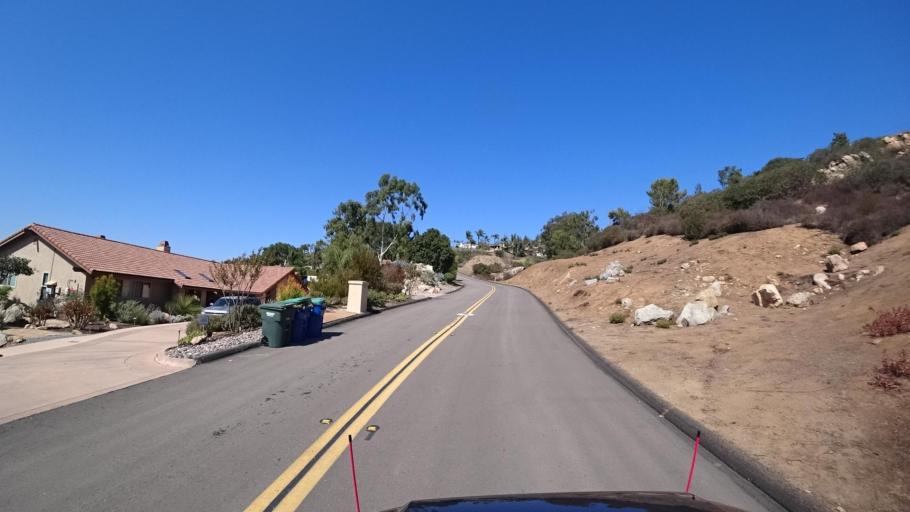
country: US
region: California
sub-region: San Diego County
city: Granite Hills
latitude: 32.8014
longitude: -116.8950
